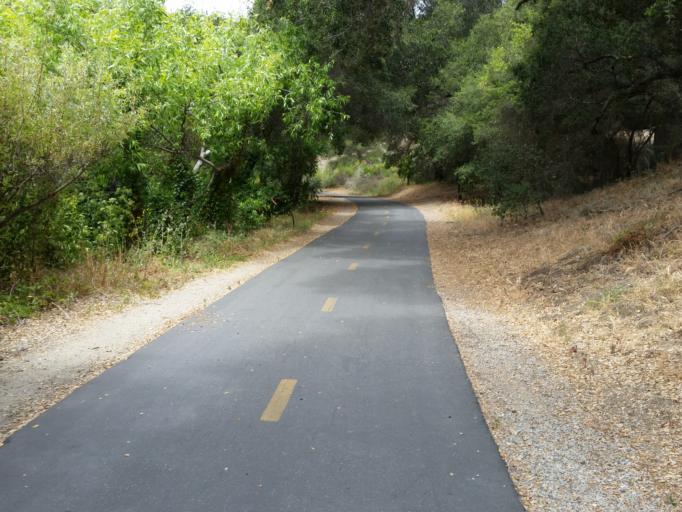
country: US
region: California
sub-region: San Luis Obispo County
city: Avila Beach
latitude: 35.1859
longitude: -120.7074
